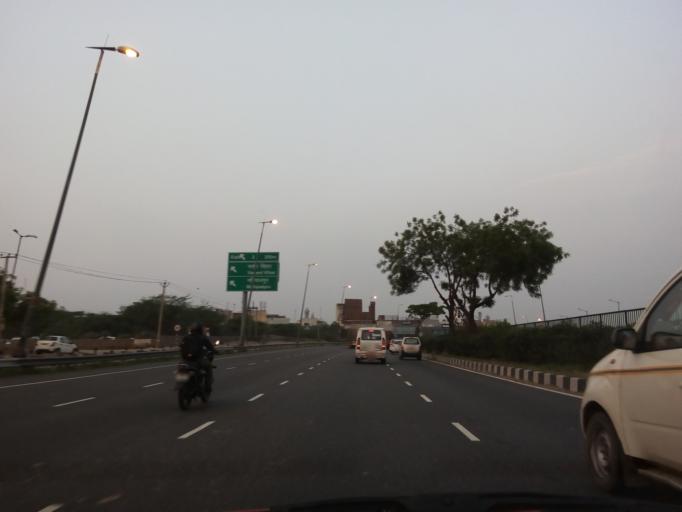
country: IN
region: NCT
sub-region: Central Delhi
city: Karol Bagh
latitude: 28.5537
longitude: 77.1318
